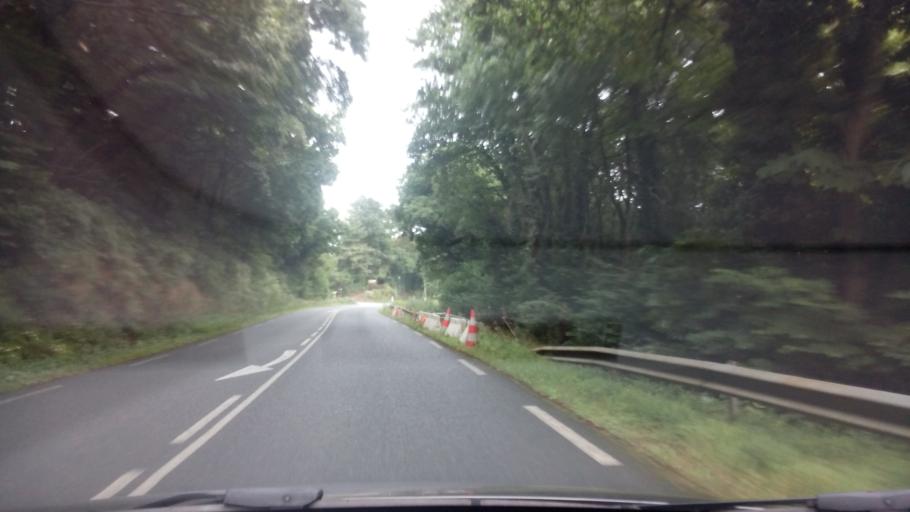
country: FR
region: Brittany
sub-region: Departement du Finistere
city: Morlaix
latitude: 48.6053
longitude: -3.7983
